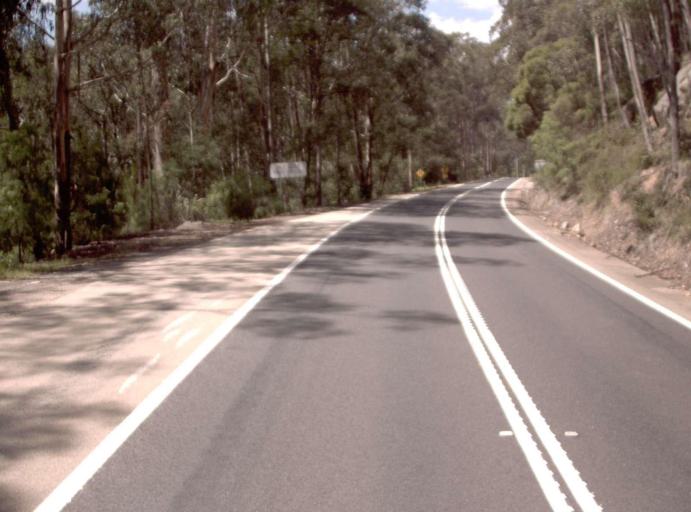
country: AU
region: New South Wales
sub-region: Bombala
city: Bombala
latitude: -37.5644
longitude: 149.3447
